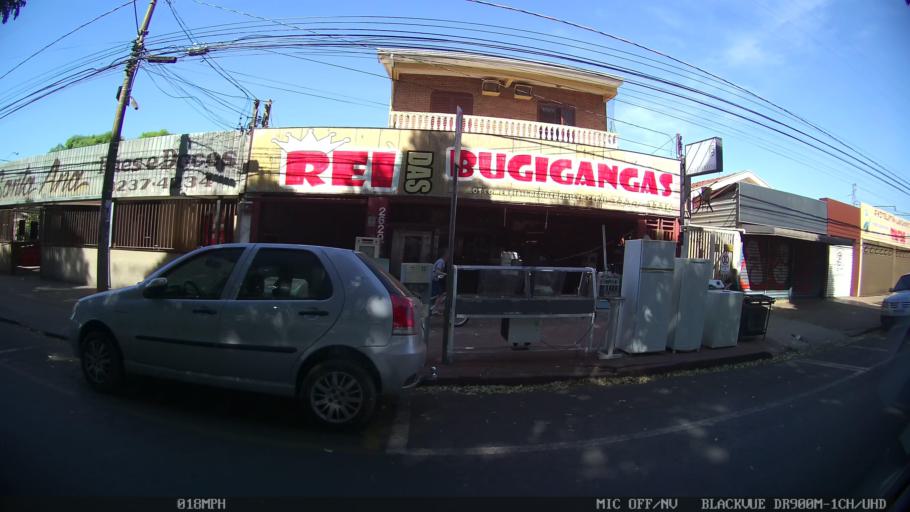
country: BR
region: Sao Paulo
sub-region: Sao Jose Do Rio Preto
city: Sao Jose do Rio Preto
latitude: -20.7856
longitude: -49.3981
